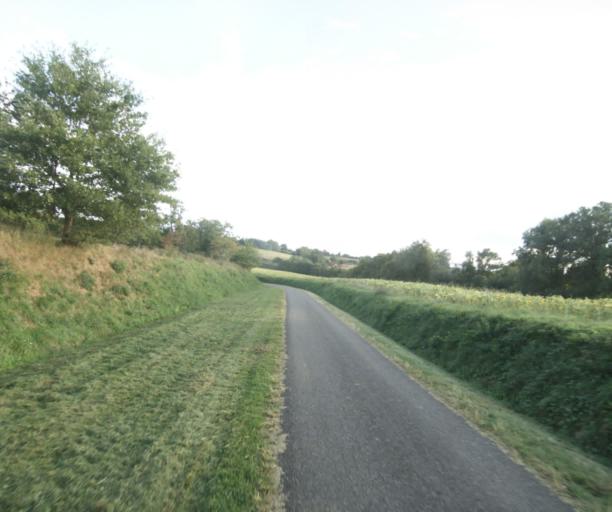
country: FR
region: Midi-Pyrenees
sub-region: Departement du Gers
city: Le Houga
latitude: 43.8479
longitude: -0.1262
